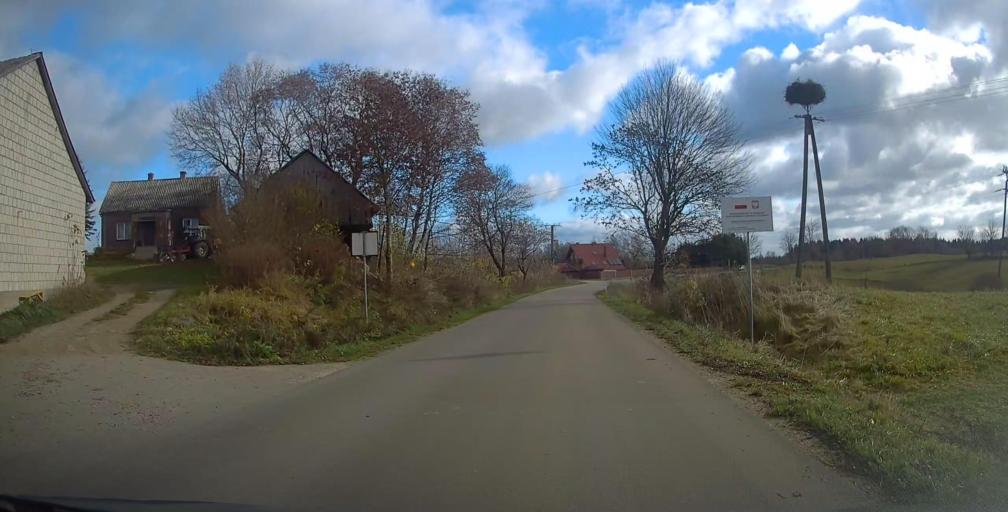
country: PL
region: Podlasie
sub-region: Suwalki
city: Suwalki
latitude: 54.3161
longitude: 22.8751
